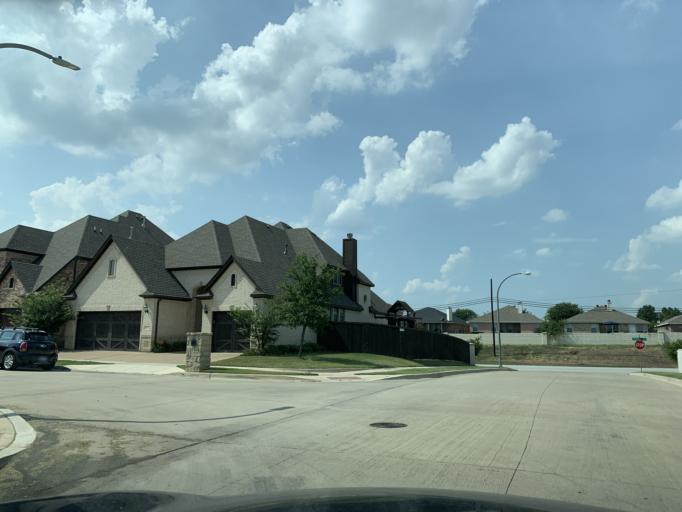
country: US
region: Texas
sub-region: Tarrant County
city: Hurst
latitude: 32.8021
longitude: -97.1960
